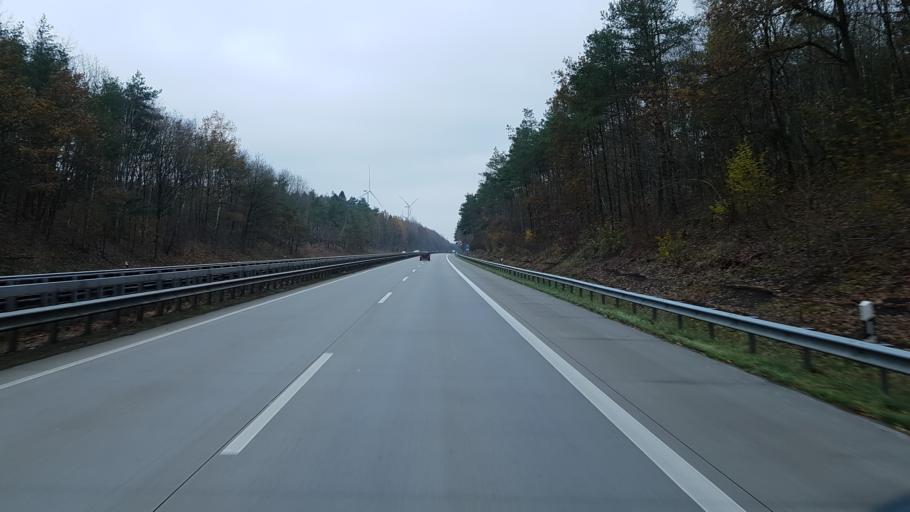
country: DE
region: Lower Saxony
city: Schwanewede
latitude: 53.2399
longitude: 8.6377
